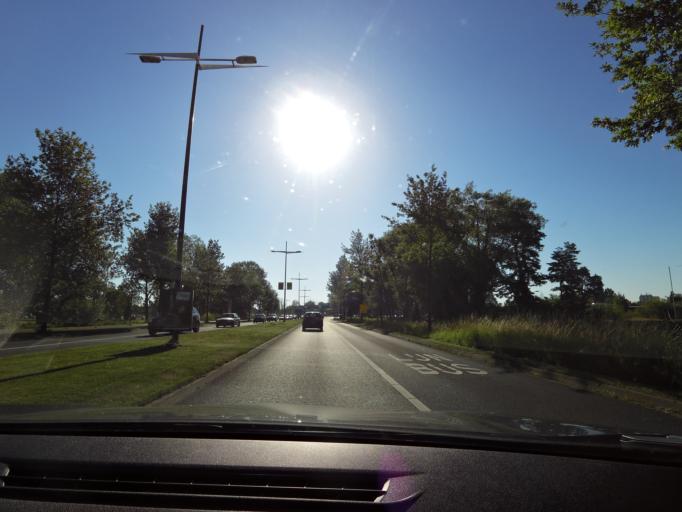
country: NL
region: Overijssel
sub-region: Gemeente Deventer
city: Deventer
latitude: 52.2536
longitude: 6.1759
